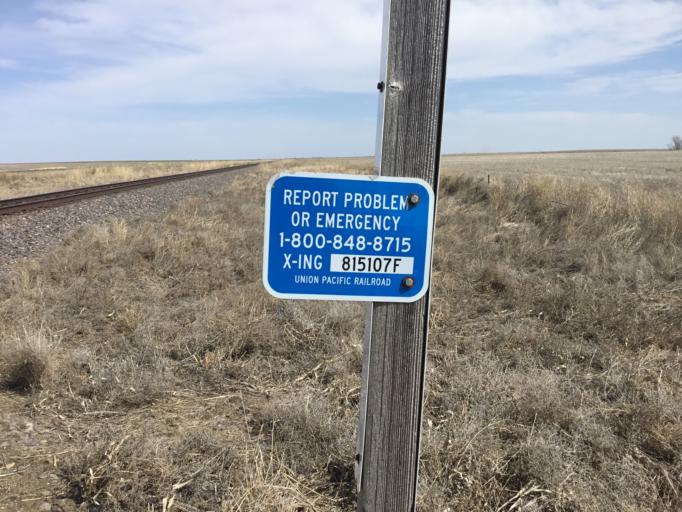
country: US
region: Kansas
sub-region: Trego County
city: WaKeeney
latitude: 39.0492
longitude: -100.0011
